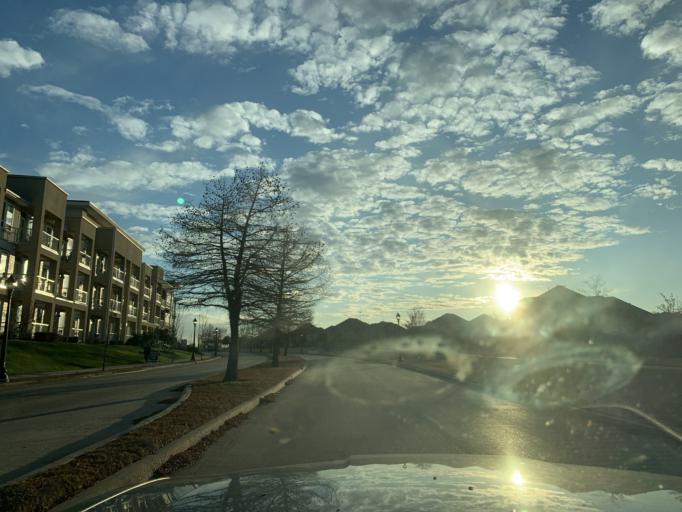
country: US
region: Texas
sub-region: Tarrant County
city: Euless
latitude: 32.8422
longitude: -97.0688
